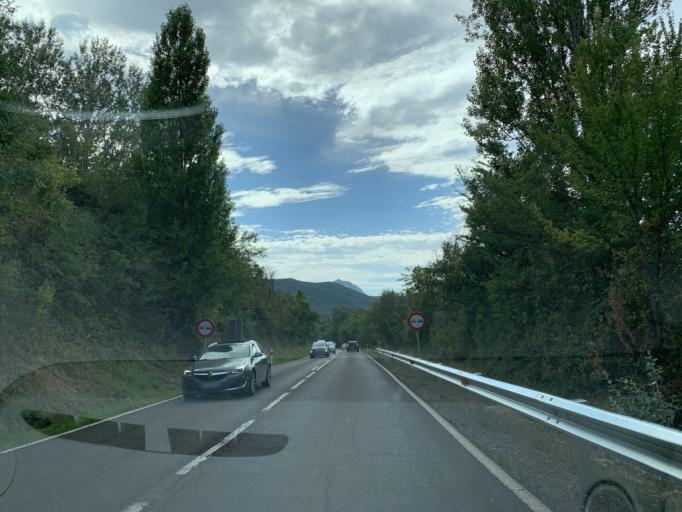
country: ES
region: Aragon
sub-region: Provincia de Huesca
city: Jaca
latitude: 42.5612
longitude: -0.5854
